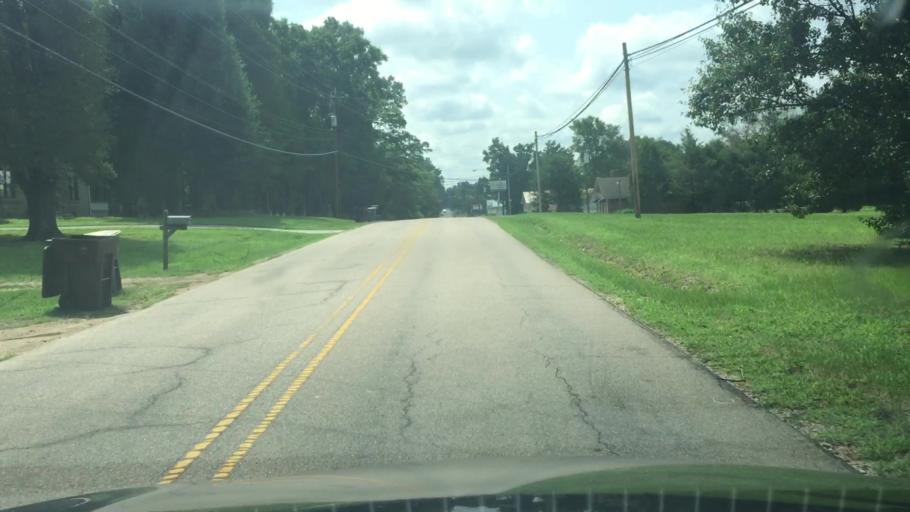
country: US
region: North Carolina
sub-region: Cabarrus County
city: Kannapolis
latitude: 35.4730
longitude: -80.6222
